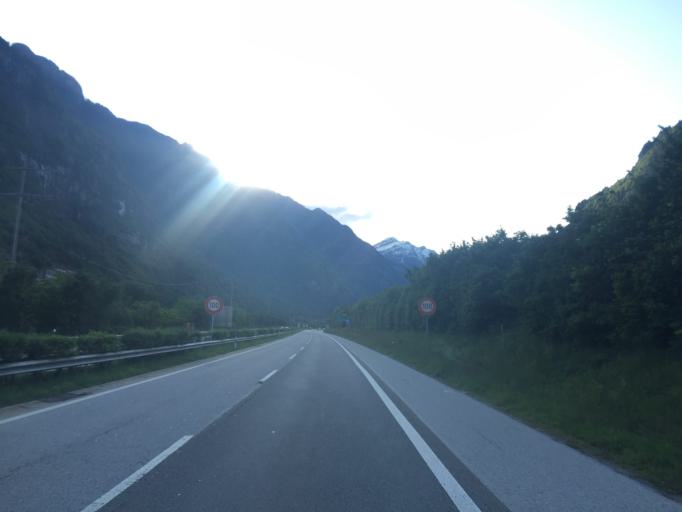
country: CH
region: Ticino
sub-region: Riviera District
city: Biasca
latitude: 46.3602
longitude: 8.9485
